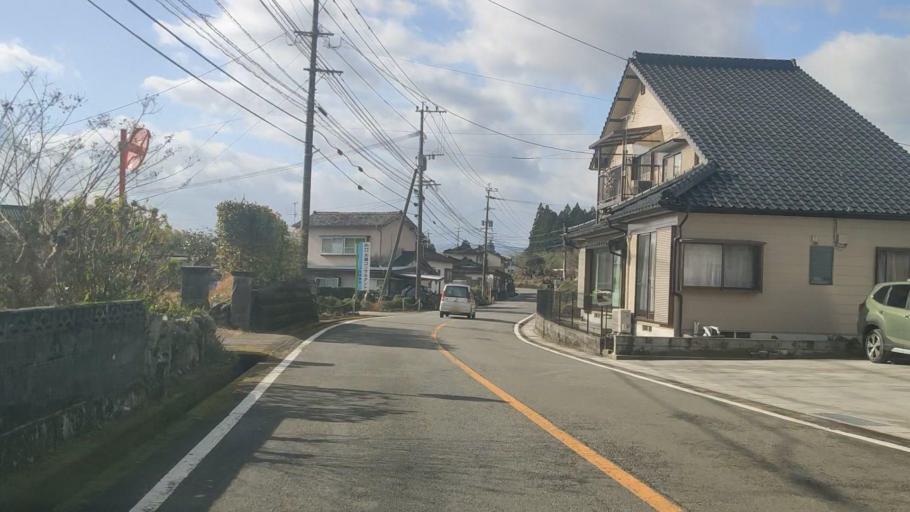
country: JP
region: Kumamoto
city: Hitoyoshi
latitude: 32.2323
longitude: 130.7869
